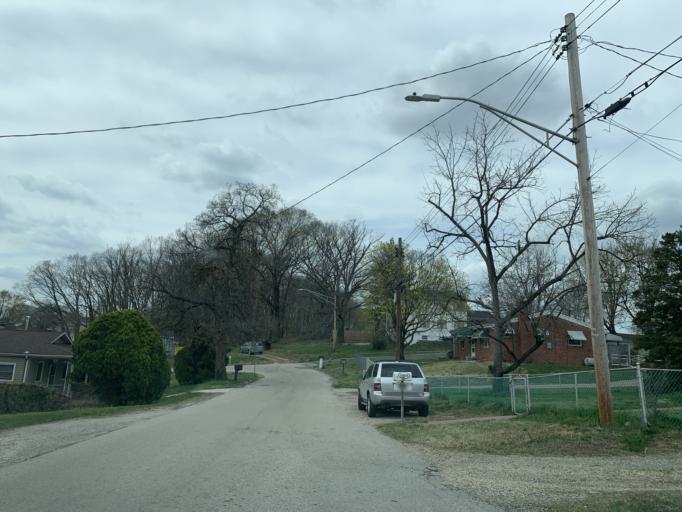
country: US
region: Maryland
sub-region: Baltimore County
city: Baltimore Highlands
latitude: 39.2414
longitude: -76.6328
